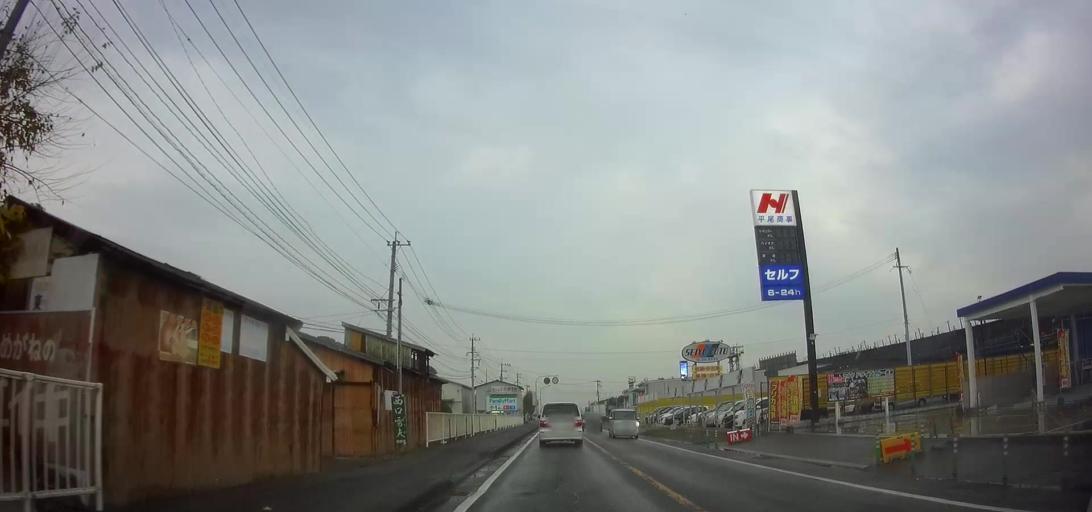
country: JP
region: Nagasaki
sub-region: Isahaya-shi
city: Isahaya
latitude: 32.8358
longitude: 130.1086
